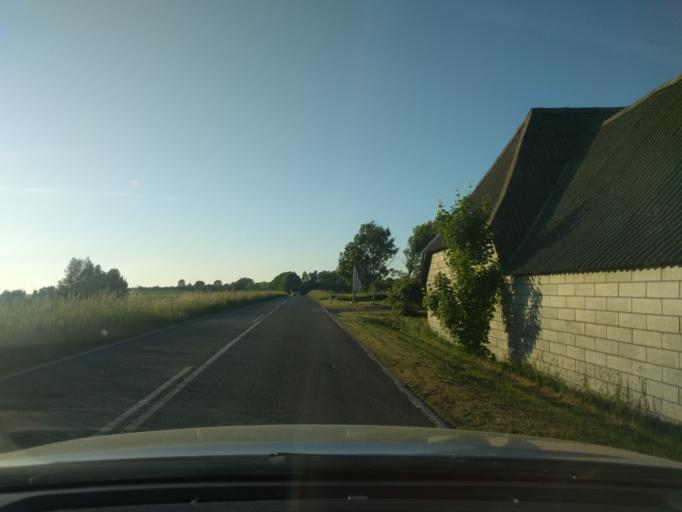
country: DK
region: South Denmark
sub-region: Kerteminde Kommune
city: Kerteminde
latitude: 55.5547
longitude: 10.6542
